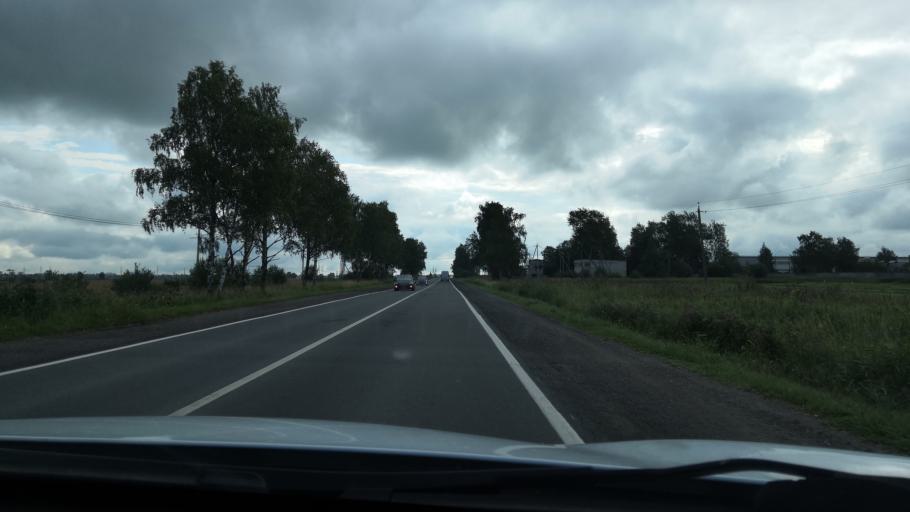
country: RU
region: St.-Petersburg
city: Tyarlevo
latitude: 59.7096
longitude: 30.4936
